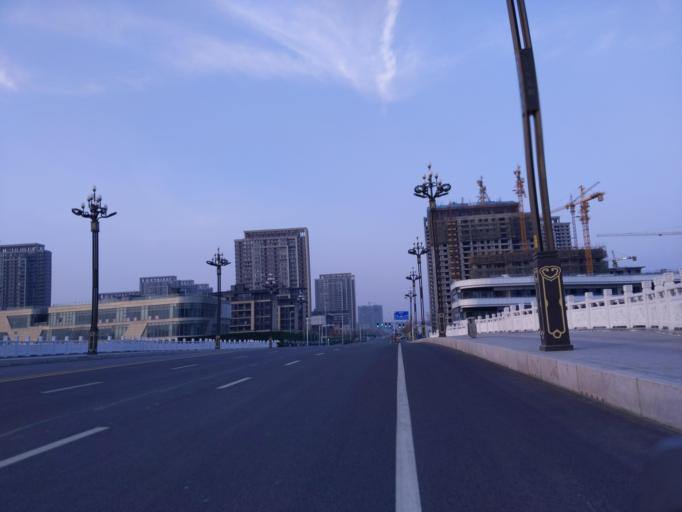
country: CN
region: Henan Sheng
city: Puyang
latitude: 35.8024
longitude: 115.0110
